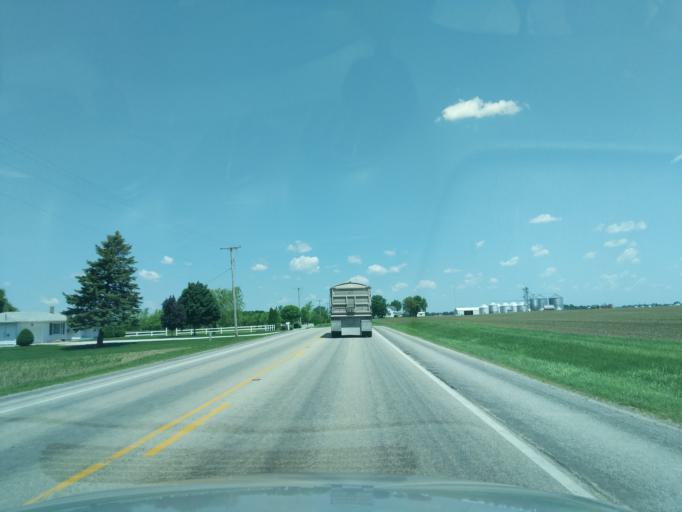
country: US
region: Indiana
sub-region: Noble County
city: Ligonier
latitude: 41.4879
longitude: -85.5775
